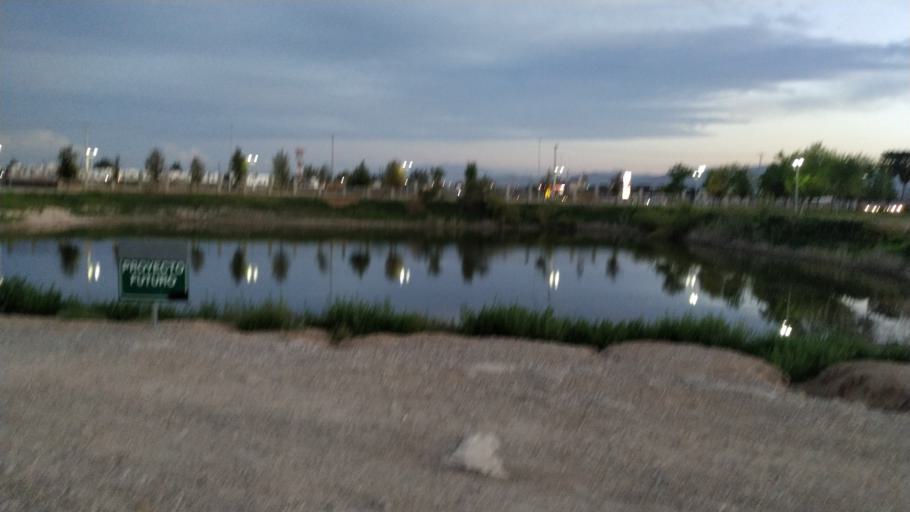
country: MX
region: Coahuila
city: Torreon
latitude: 25.5485
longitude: -103.3902
